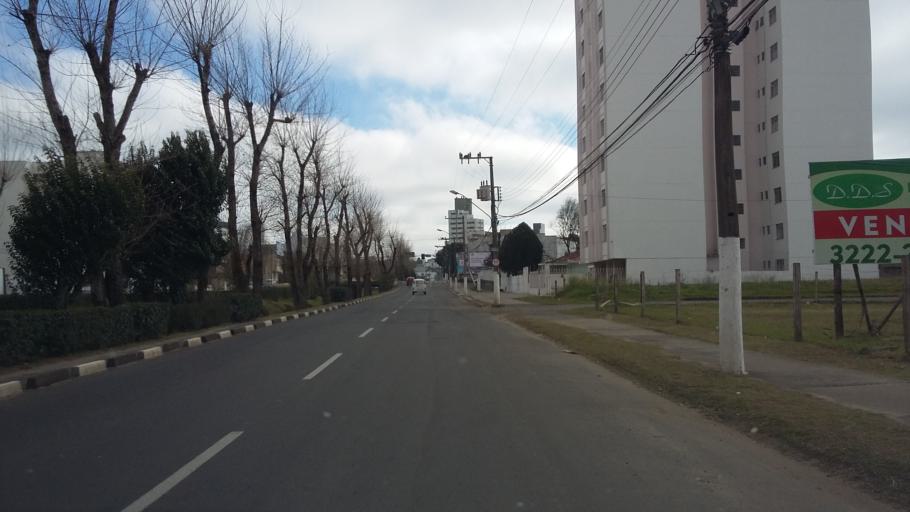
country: BR
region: Santa Catarina
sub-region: Lages
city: Lages
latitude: -27.8127
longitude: -50.3171
